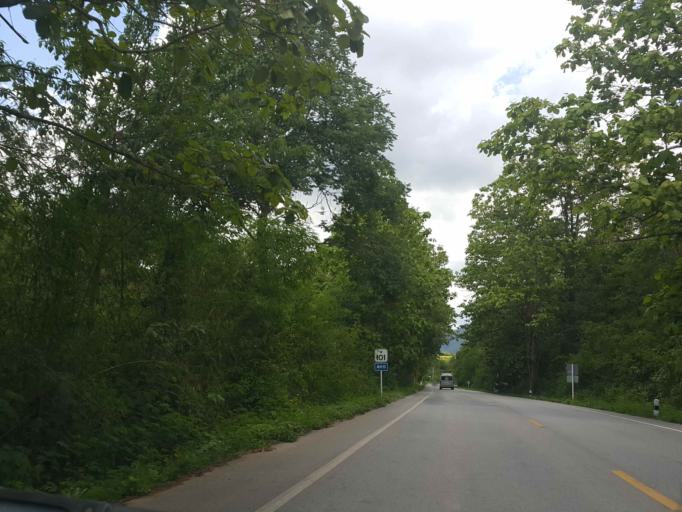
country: TH
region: Nan
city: Wiang Sa
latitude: 18.5218
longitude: 100.5801
